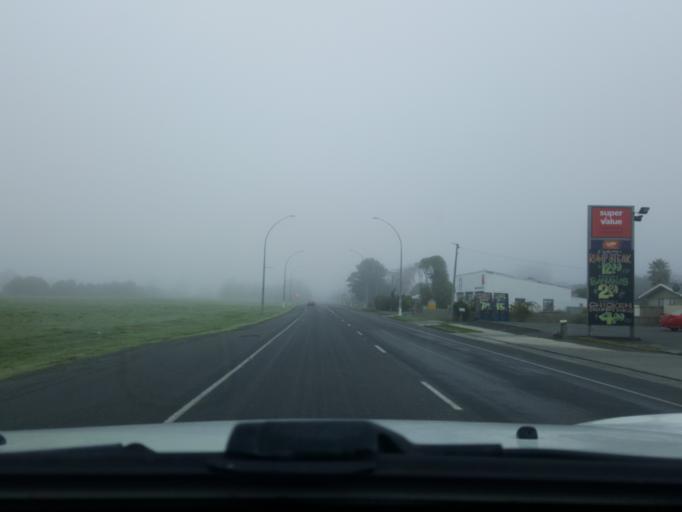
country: NZ
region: Waikato
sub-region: Waikato District
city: Ngaruawahia
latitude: -37.6749
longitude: 175.1580
